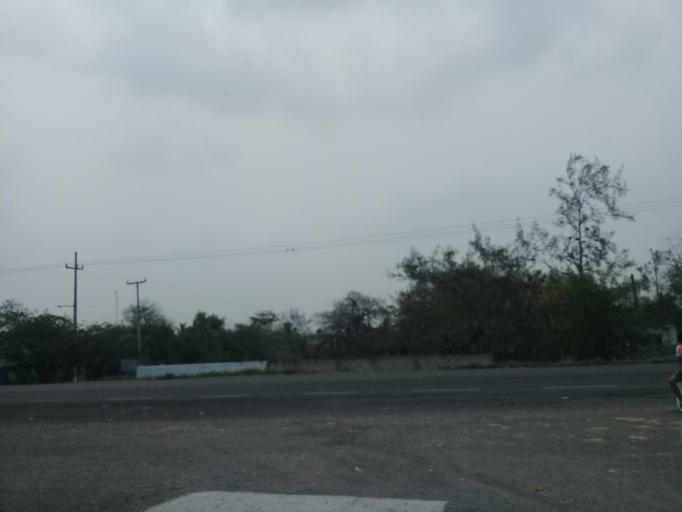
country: MX
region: Veracruz
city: Jamapa
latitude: 18.9168
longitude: -96.1977
